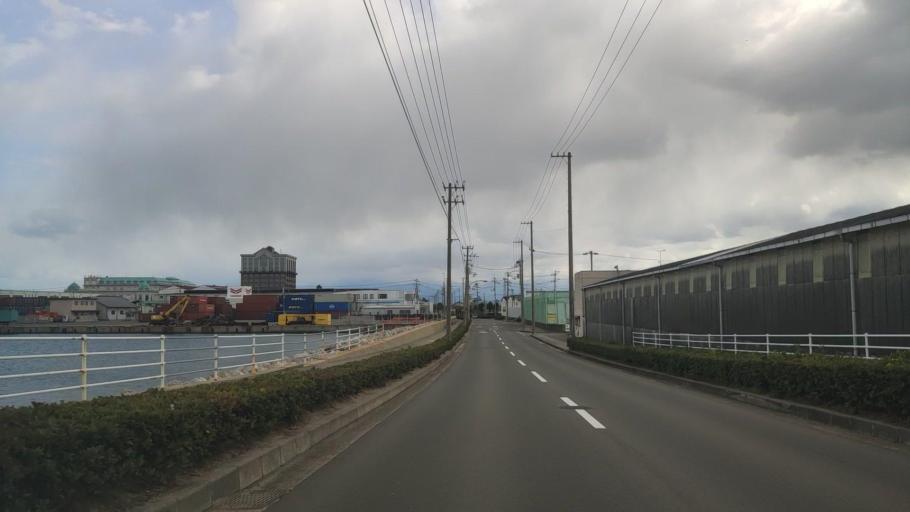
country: JP
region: Ehime
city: Saijo
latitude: 34.0511
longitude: 133.0240
